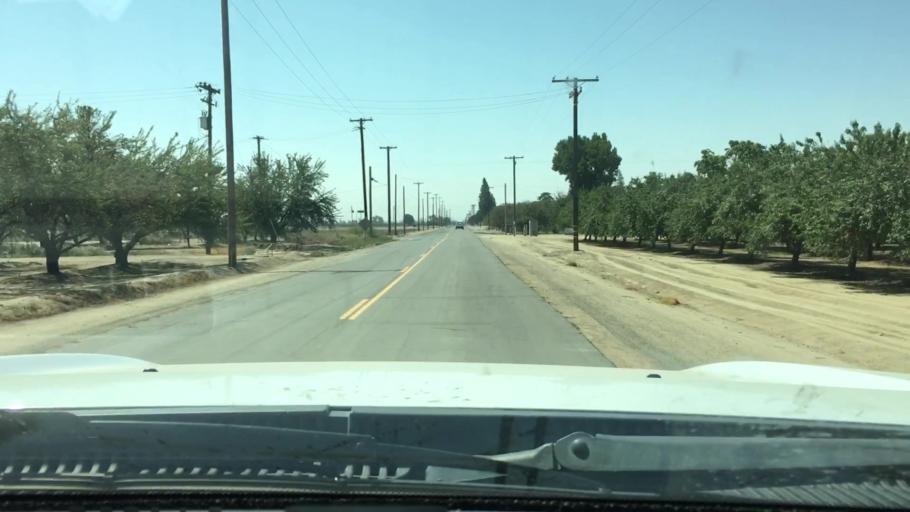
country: US
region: California
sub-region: Kern County
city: Shafter
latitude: 35.5373
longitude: -119.2778
